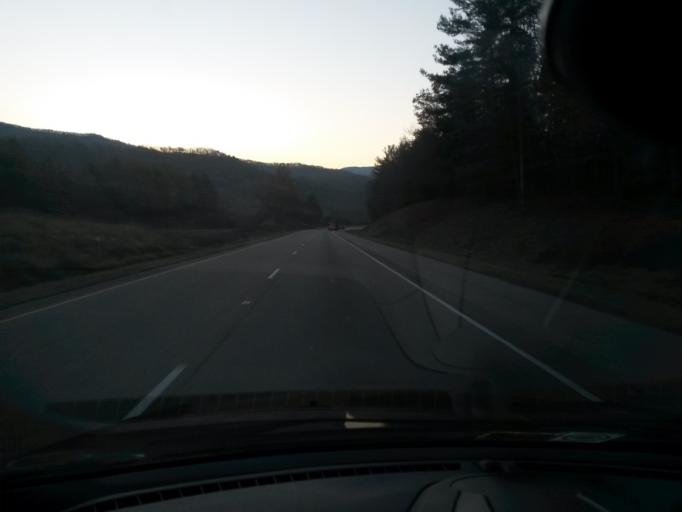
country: US
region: Virginia
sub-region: Alleghany County
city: Clifton Forge
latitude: 37.8226
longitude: -79.7460
